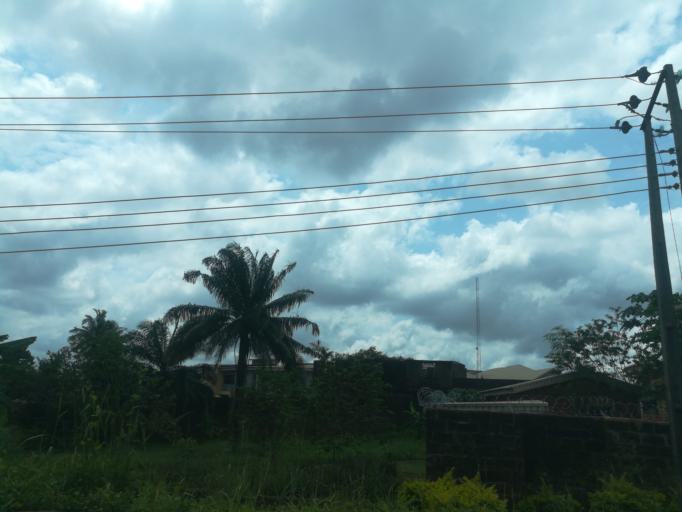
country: NG
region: Oyo
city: Ibadan
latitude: 7.3662
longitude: 3.8327
